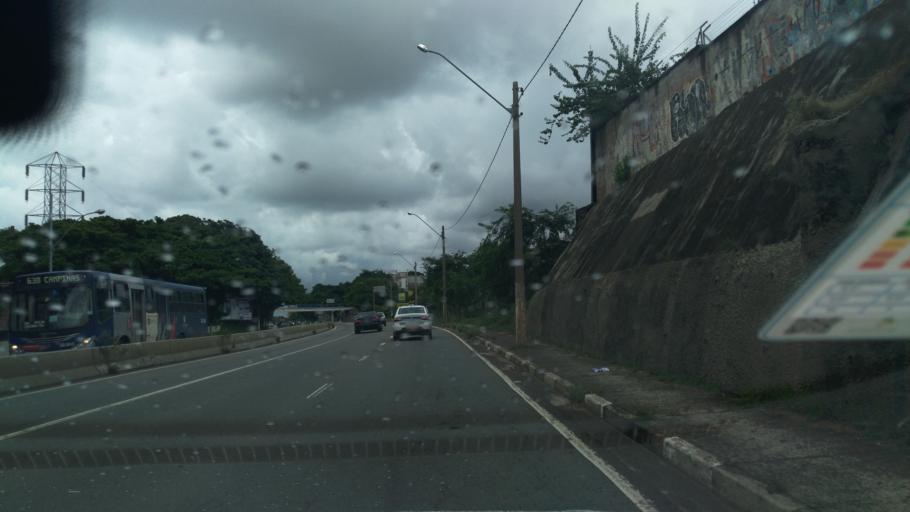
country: BR
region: Sao Paulo
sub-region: Campinas
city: Campinas
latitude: -22.9007
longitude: -47.0834
